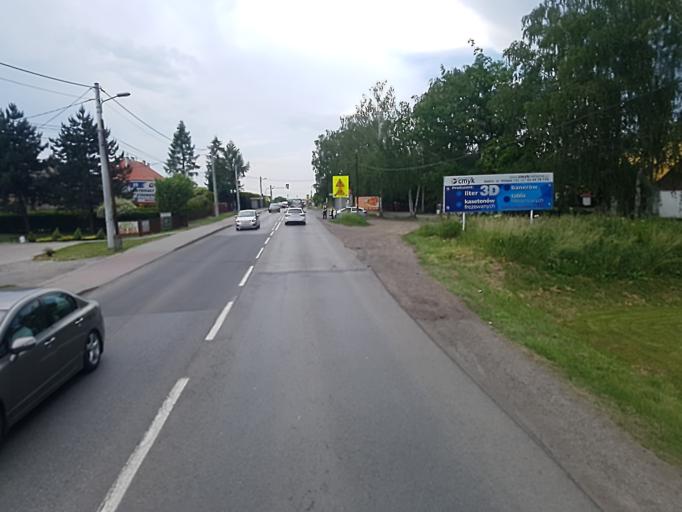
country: PL
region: Silesian Voivodeship
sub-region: Powiat wodzislawski
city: Wodzislaw Slaski
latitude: 49.9900
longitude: 18.4956
